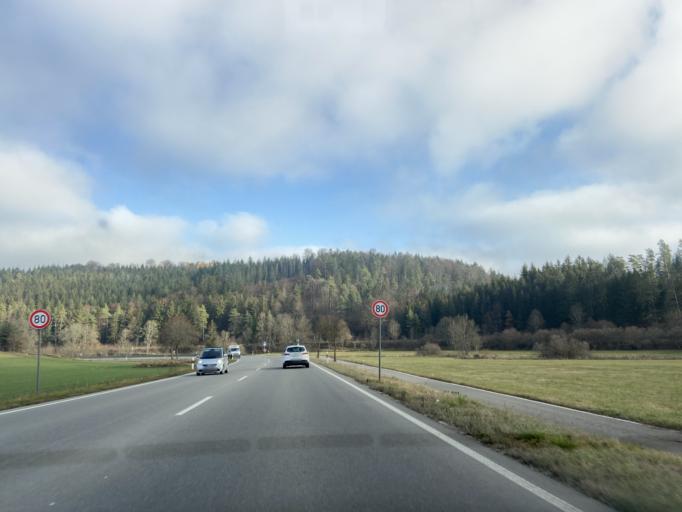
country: DE
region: Baden-Wuerttemberg
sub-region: Tuebingen Region
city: Gammertingen
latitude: 48.2679
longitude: 9.2140
